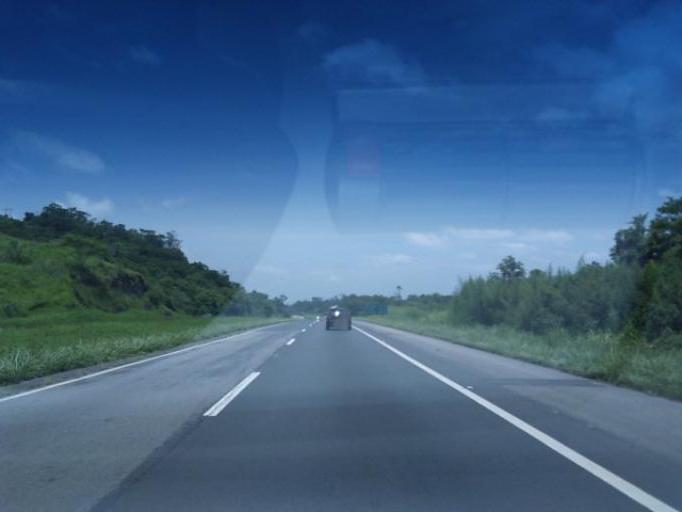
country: BR
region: Sao Paulo
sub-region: Miracatu
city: Miracatu
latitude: -24.2637
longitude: -47.3829
